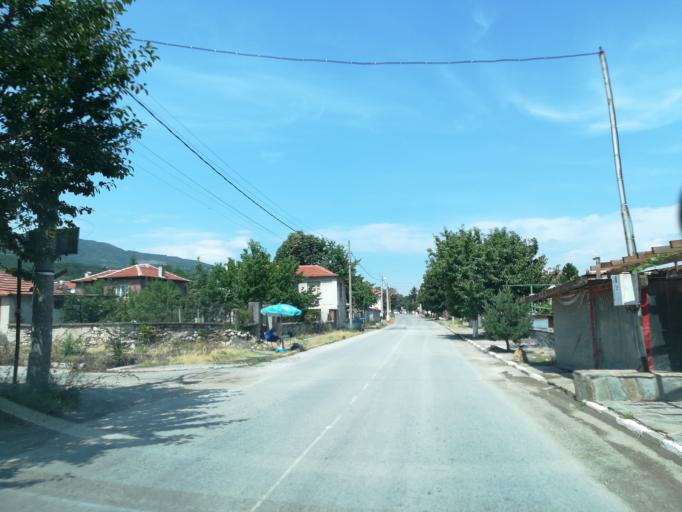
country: BG
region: Plovdiv
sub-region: Obshtina Asenovgrad
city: Asenovgrad
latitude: 41.9466
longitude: 24.9602
